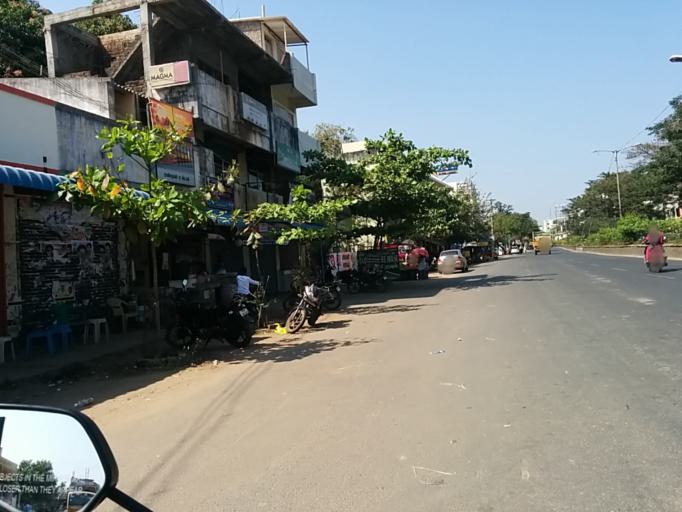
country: IN
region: Pondicherry
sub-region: Puducherry
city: Puducherry
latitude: 11.9387
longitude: 79.8079
